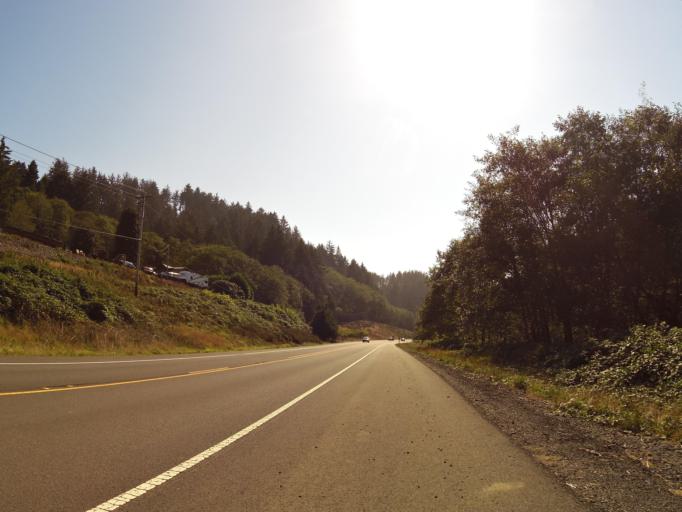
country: US
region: Oregon
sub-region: Tillamook County
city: Pacific City
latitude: 45.1527
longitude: -123.9558
